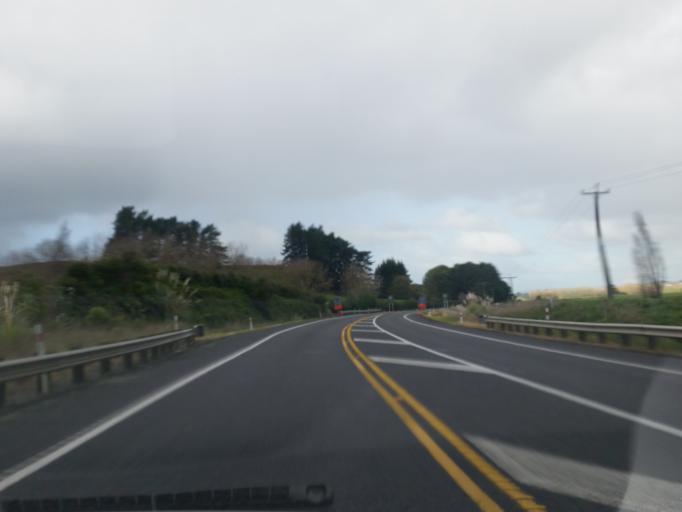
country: NZ
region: Auckland
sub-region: Auckland
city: Pukekohe East
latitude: -37.2117
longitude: 175.0805
